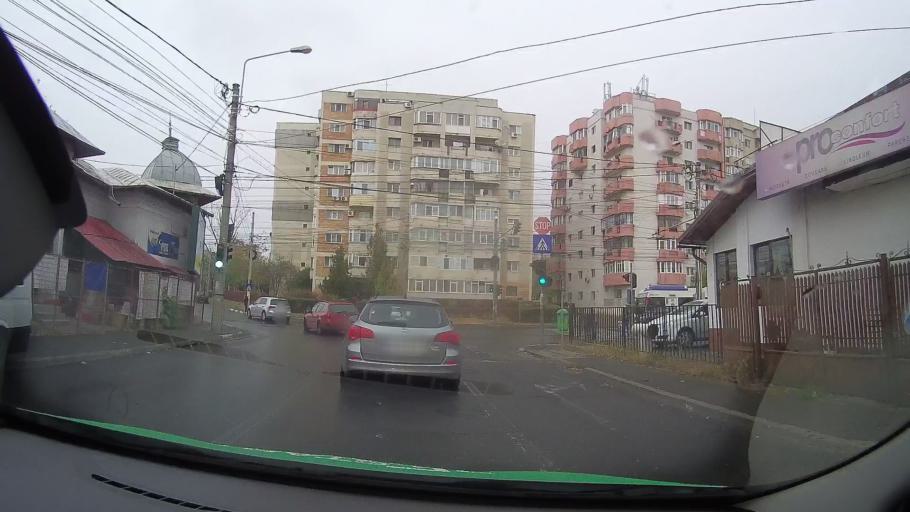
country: RO
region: Prahova
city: Ploiesti
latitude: 44.9375
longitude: 26.0045
